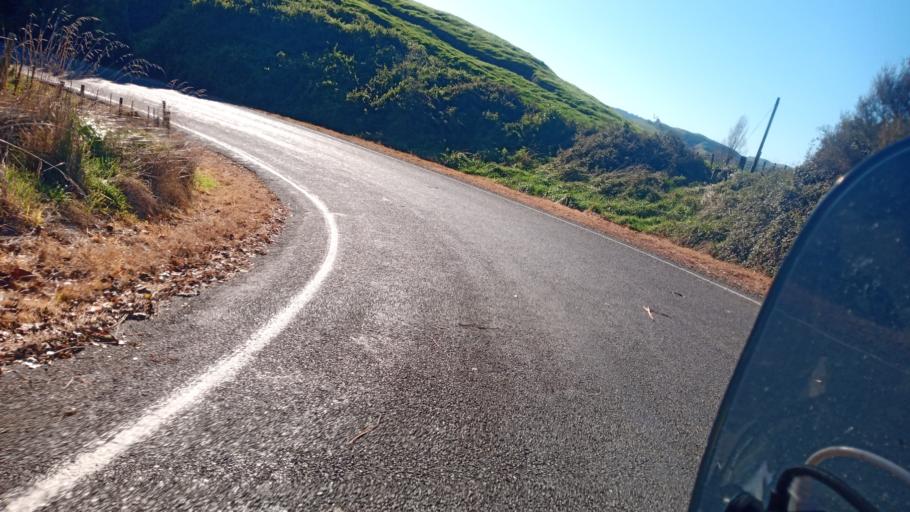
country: NZ
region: Hawke's Bay
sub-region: Wairoa District
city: Wairoa
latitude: -38.8217
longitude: 177.2928
